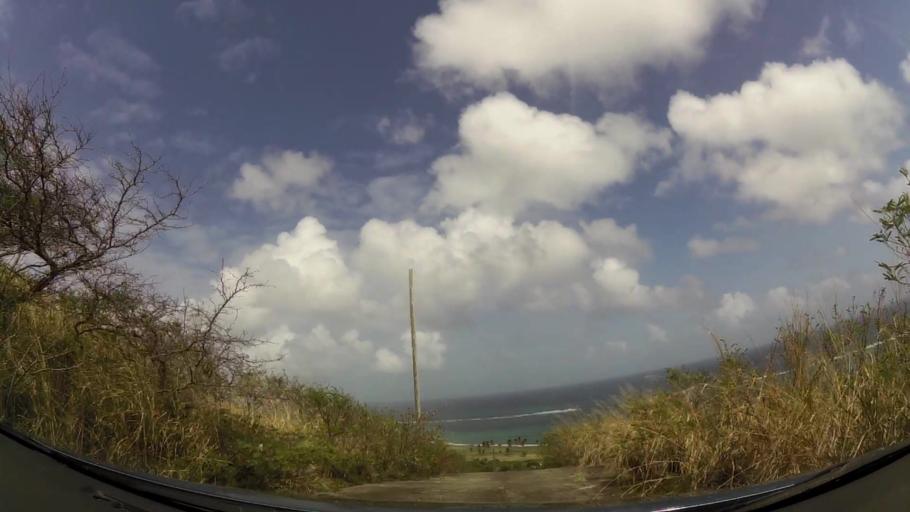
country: KN
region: Saint Peter Basseterre
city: Monkey Hill
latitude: 17.3000
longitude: -62.6935
